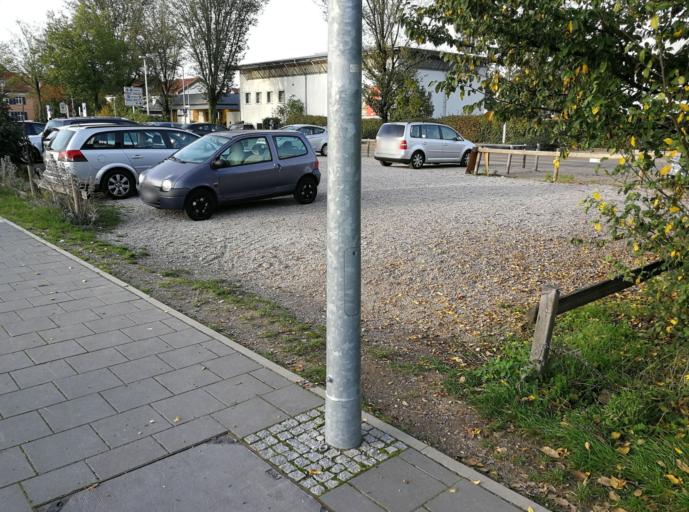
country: DE
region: Baden-Wuerttemberg
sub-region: Freiburg Region
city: Oberkirch
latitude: 48.5296
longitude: 8.0761
